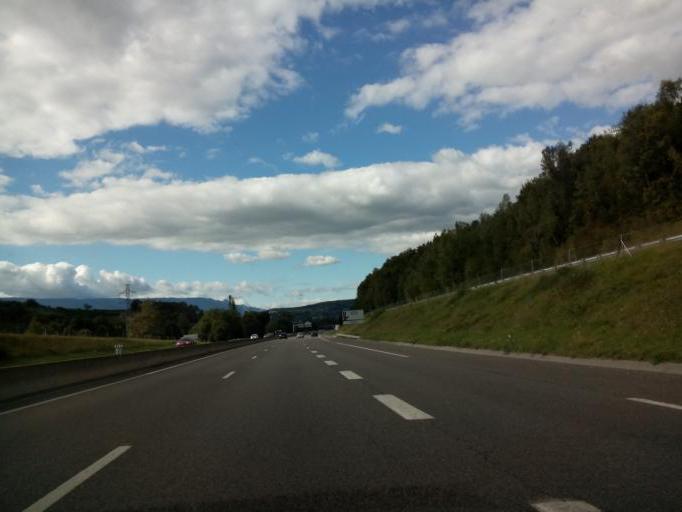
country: FR
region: Rhone-Alpes
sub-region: Departement de la Savoie
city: Saint-Baldoph
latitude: 45.5426
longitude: 5.9631
